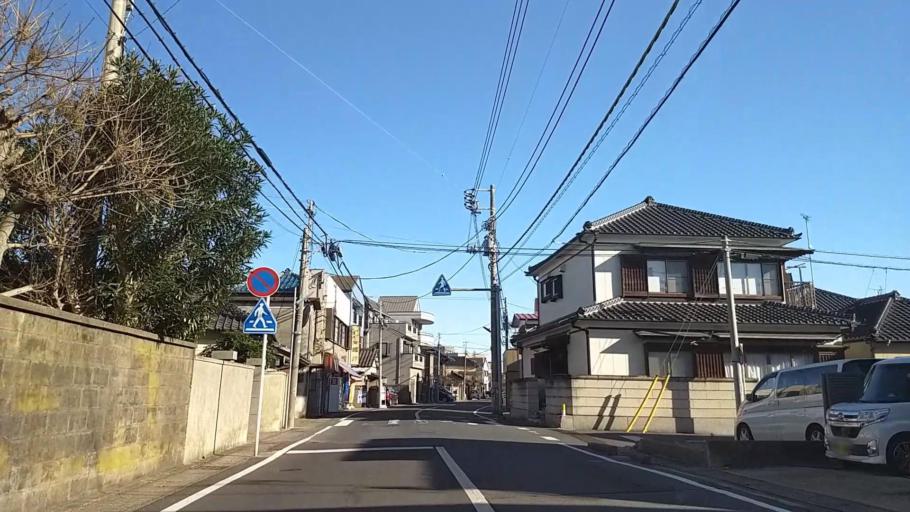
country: JP
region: Chiba
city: Hasaki
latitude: 35.7359
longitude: 140.8482
